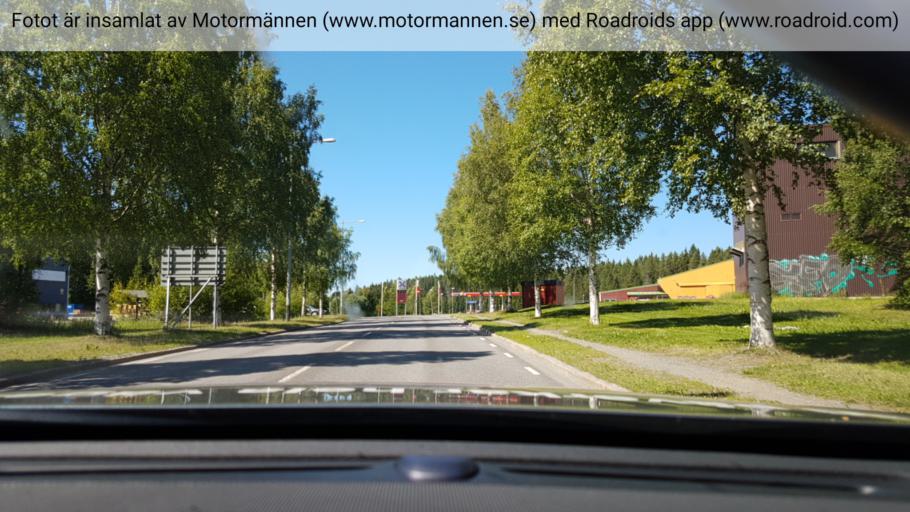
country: SE
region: Vaesterbotten
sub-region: Skelleftea Kommun
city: Skelleftea
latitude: 64.7615
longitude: 20.9506
